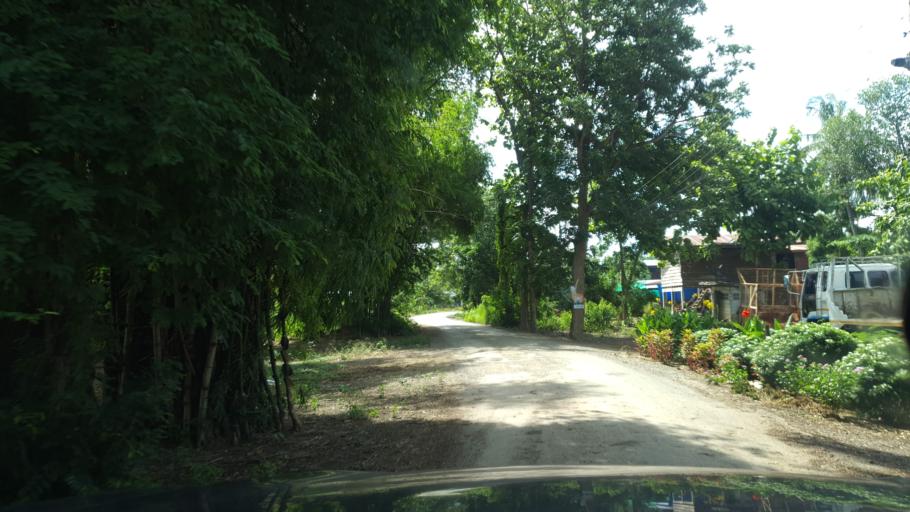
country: TH
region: Sukhothai
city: Sawankhalok
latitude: 17.2176
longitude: 99.7149
